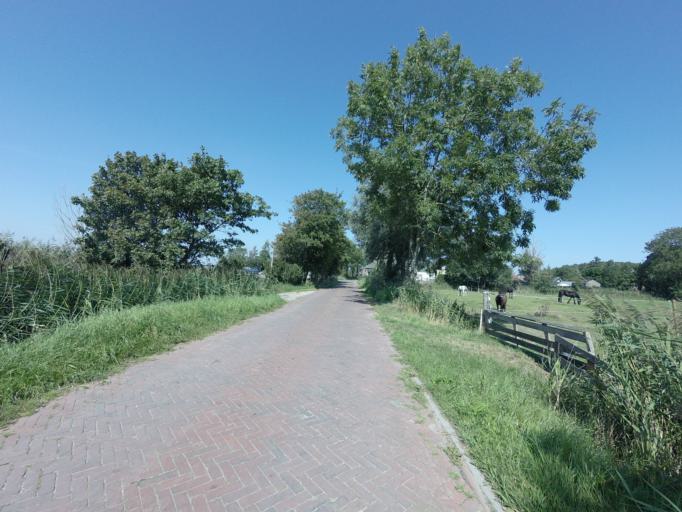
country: NL
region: Friesland
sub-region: Gemeente Dongeradeel
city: Ternaard
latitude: 53.3710
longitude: 5.9953
